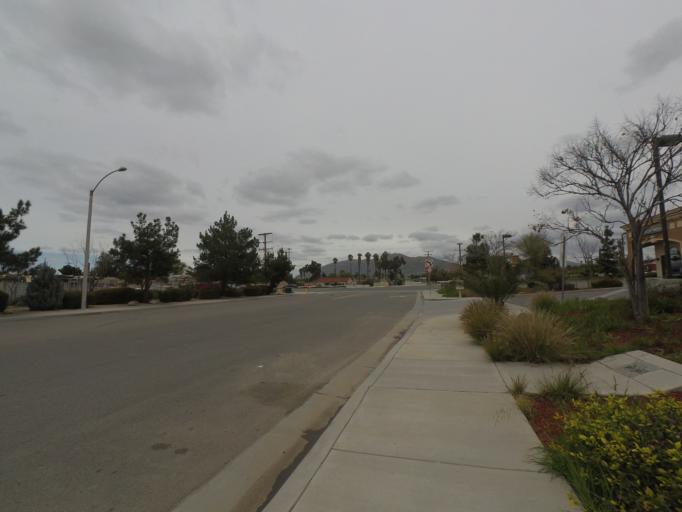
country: US
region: California
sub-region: Riverside County
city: March Air Force Base
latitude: 33.9162
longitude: -117.2741
